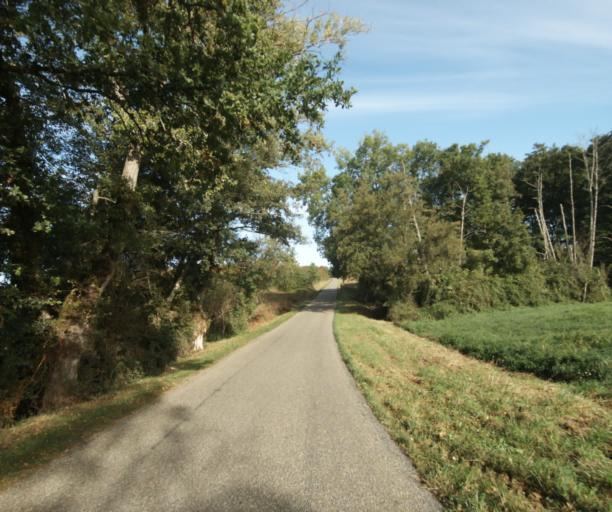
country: FR
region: Midi-Pyrenees
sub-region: Departement du Gers
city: Eauze
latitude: 43.9288
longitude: 0.1240
